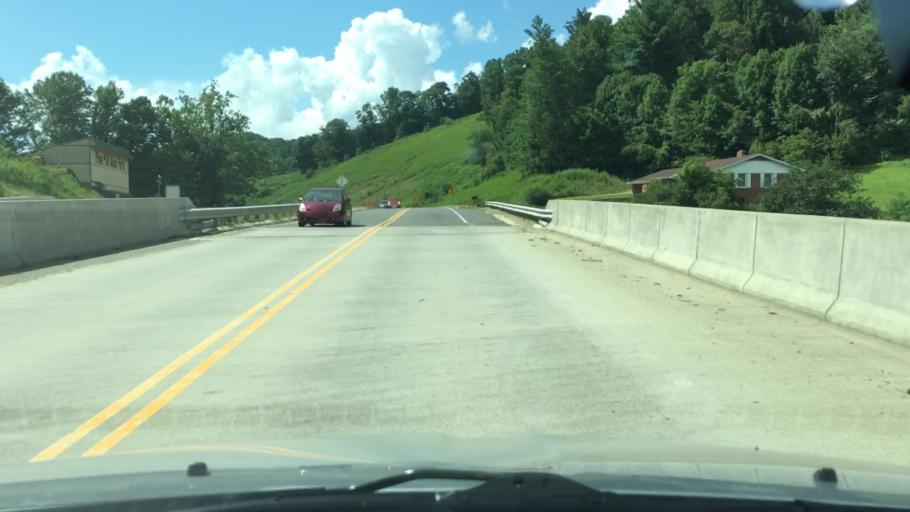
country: US
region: North Carolina
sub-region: Yancey County
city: Burnsville
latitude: 35.9096
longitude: -82.2196
